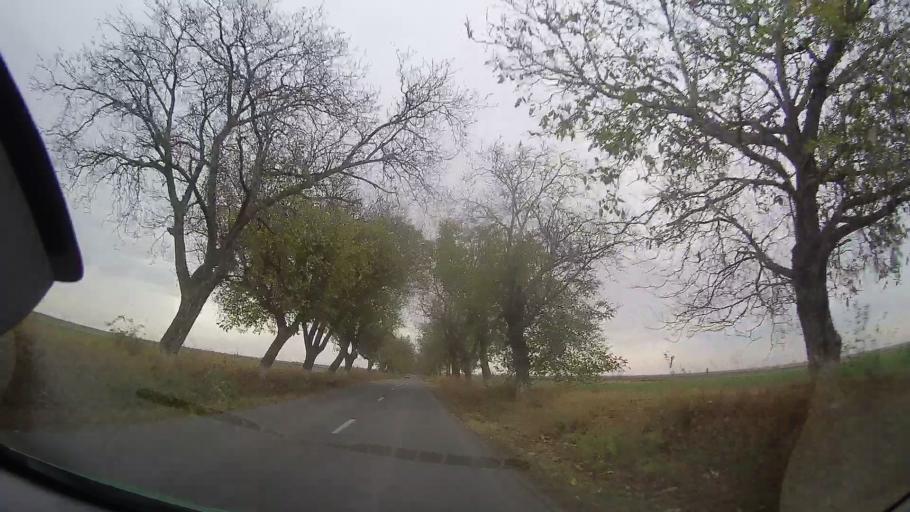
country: RO
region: Prahova
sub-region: Comuna Fantanele
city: Fantanele
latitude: 45.0174
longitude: 26.3999
